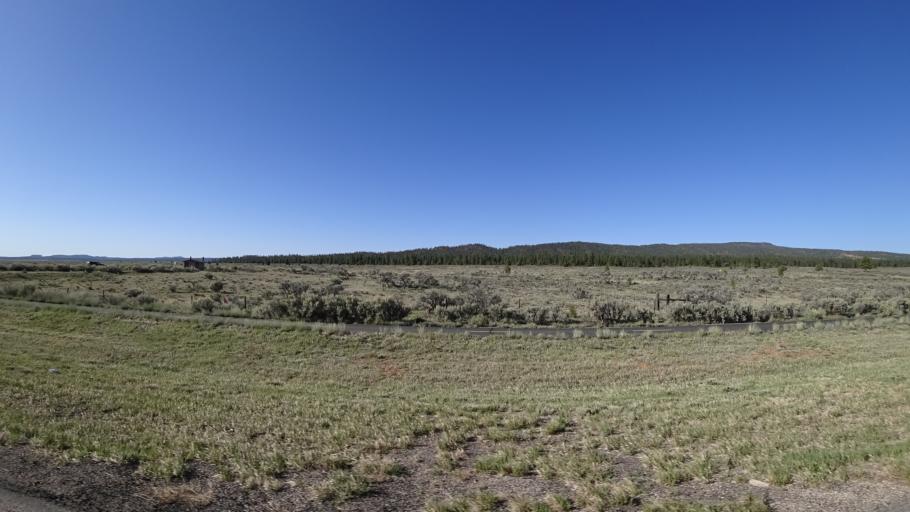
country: US
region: Utah
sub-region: Garfield County
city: Panguitch
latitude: 37.7199
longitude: -112.2576
